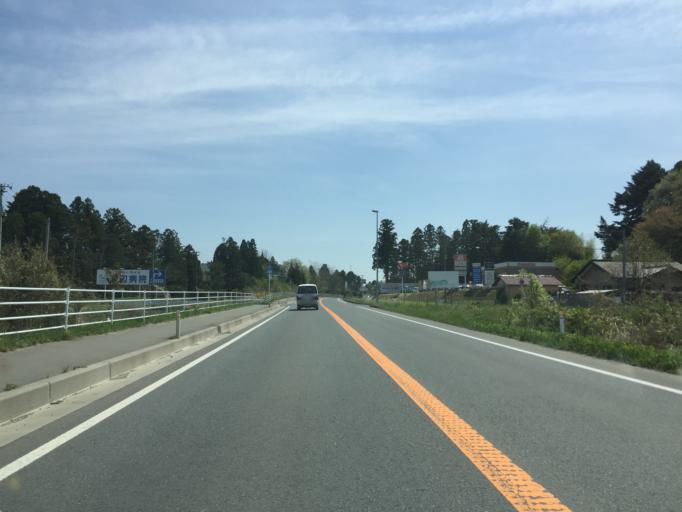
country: JP
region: Miyagi
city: Marumori
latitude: 37.8667
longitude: 140.9199
